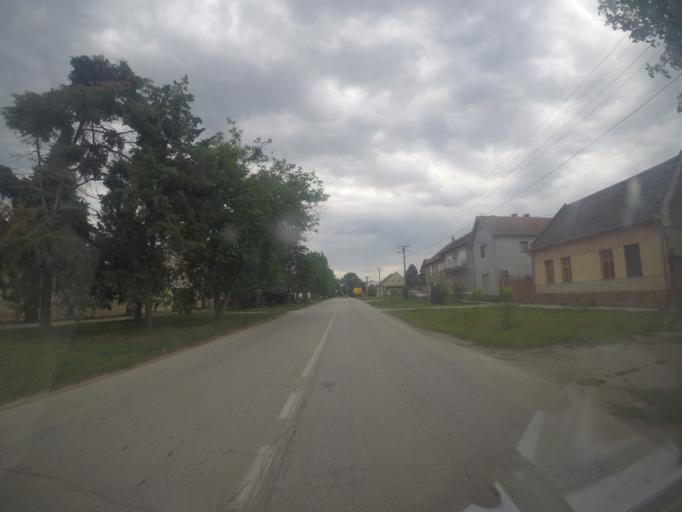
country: RS
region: Autonomna Pokrajina Vojvodina
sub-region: Juznobanatski Okrug
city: Opovo
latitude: 45.0530
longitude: 20.4184
